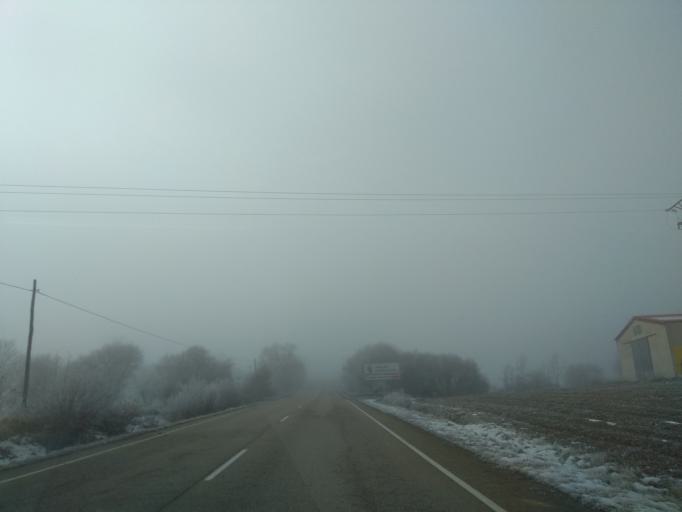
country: ES
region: Castille and Leon
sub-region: Provincia de Burgos
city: Espinosa de los Monteros
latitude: 43.0275
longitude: -3.5037
